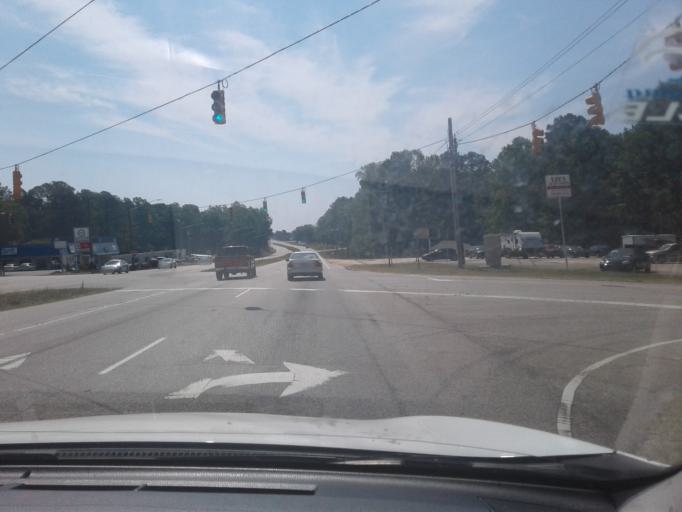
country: US
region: North Carolina
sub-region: Harnett County
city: Erwin
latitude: 35.3354
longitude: -78.6740
